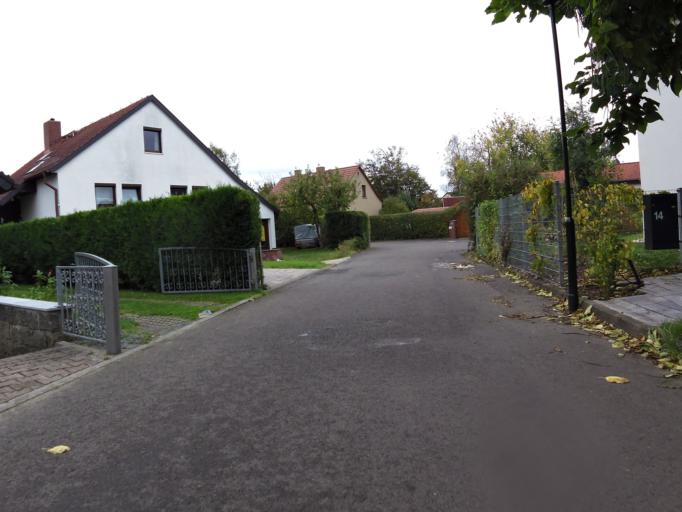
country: DE
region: Saxony
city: Markkleeberg
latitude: 51.2910
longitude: 12.3613
